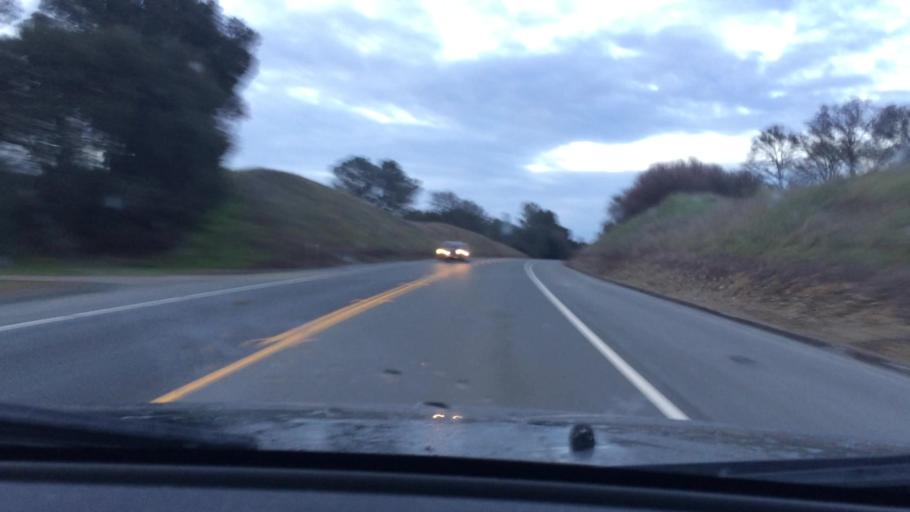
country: US
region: California
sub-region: Amador County
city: Ione
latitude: 38.4006
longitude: -120.8931
